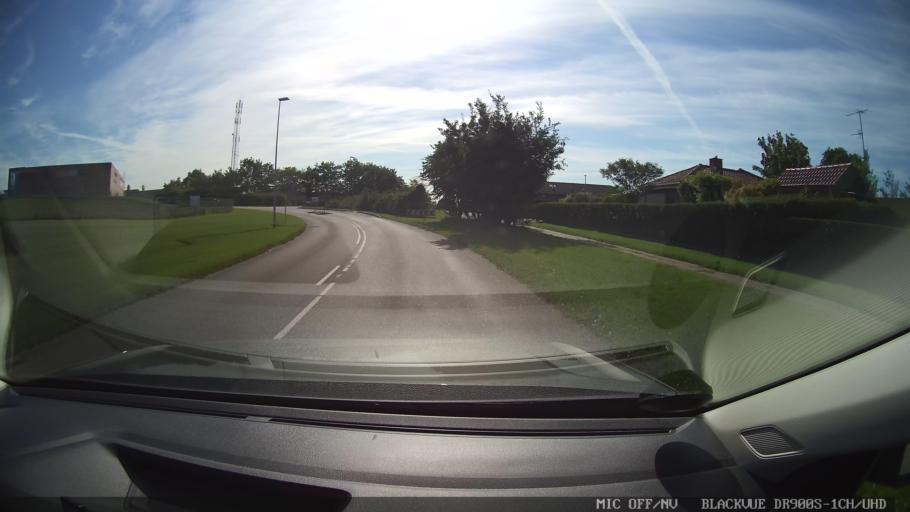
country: DK
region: North Denmark
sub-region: Mariagerfjord Kommune
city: Hobro
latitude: 56.5453
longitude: 9.8548
